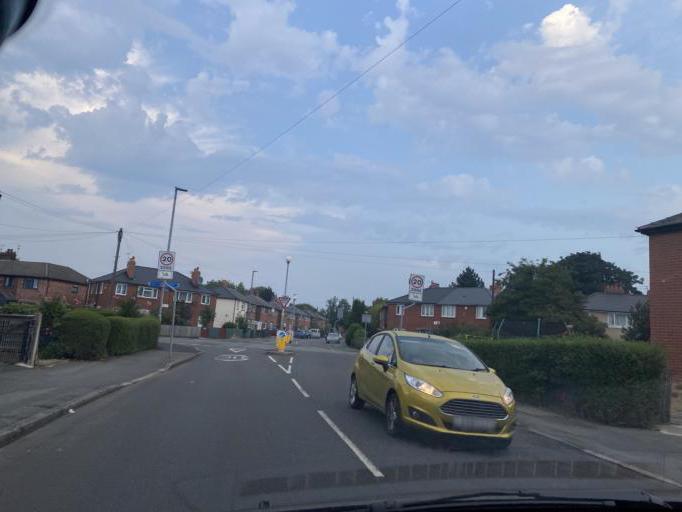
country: GB
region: England
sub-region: Manchester
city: Fallowfield
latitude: 53.4450
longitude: -2.2317
